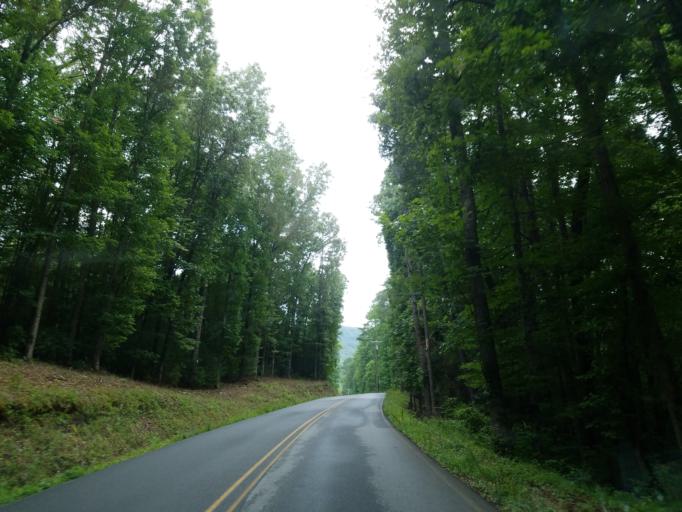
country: US
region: Georgia
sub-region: Fannin County
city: Blue Ridge
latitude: 34.7803
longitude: -84.2671
